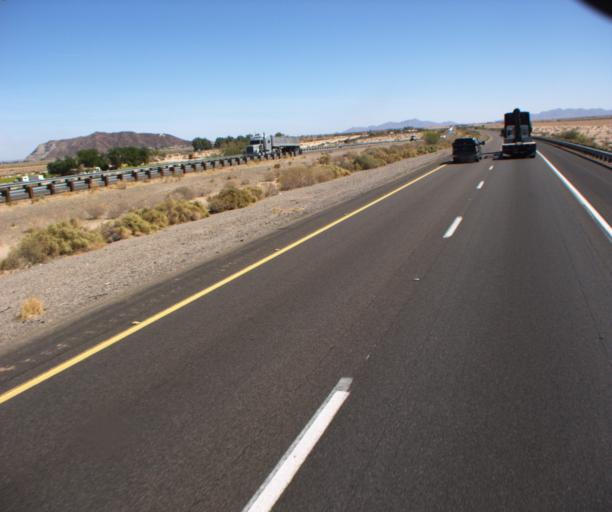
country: US
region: Arizona
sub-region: Yuma County
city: Wellton
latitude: 32.6765
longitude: -114.0468
